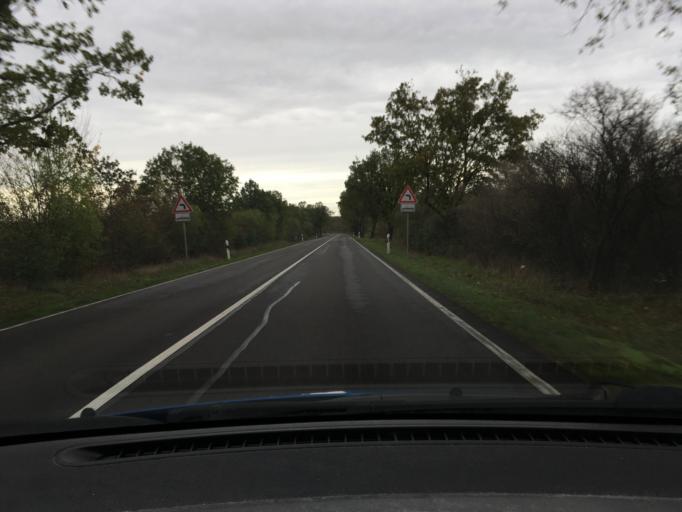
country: DE
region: Saxony-Anhalt
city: Leitzkau
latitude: 52.0306
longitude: 11.9954
